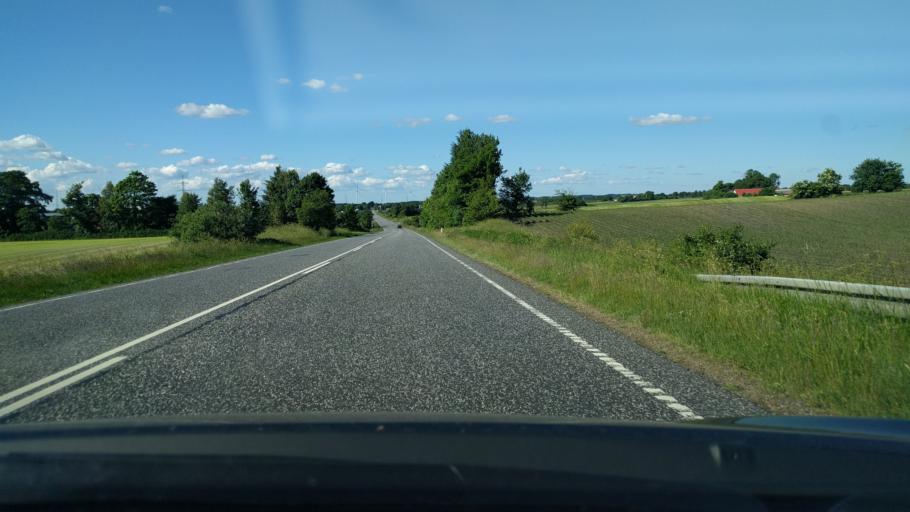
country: DK
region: North Denmark
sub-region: Vesthimmerland Kommune
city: Alestrup
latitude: 56.6524
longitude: 9.5207
